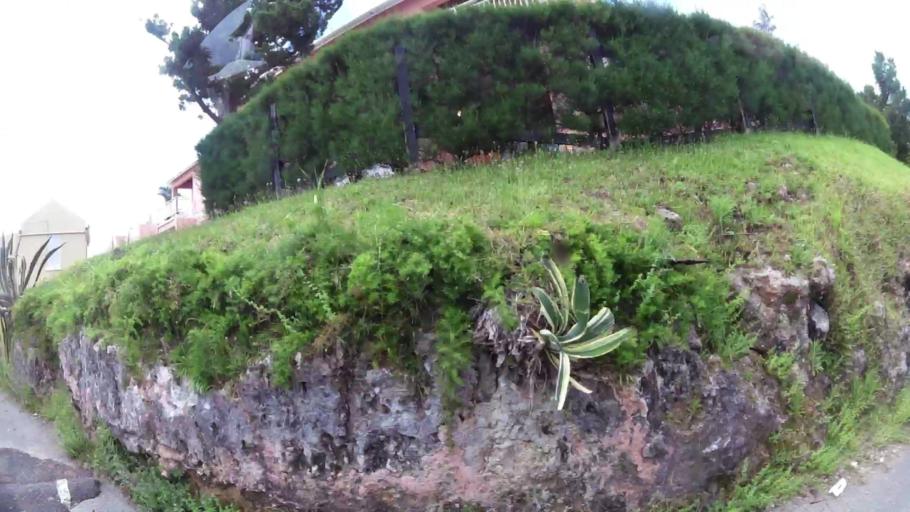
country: BM
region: Saint George
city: Saint George
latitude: 32.3686
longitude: -64.6498
